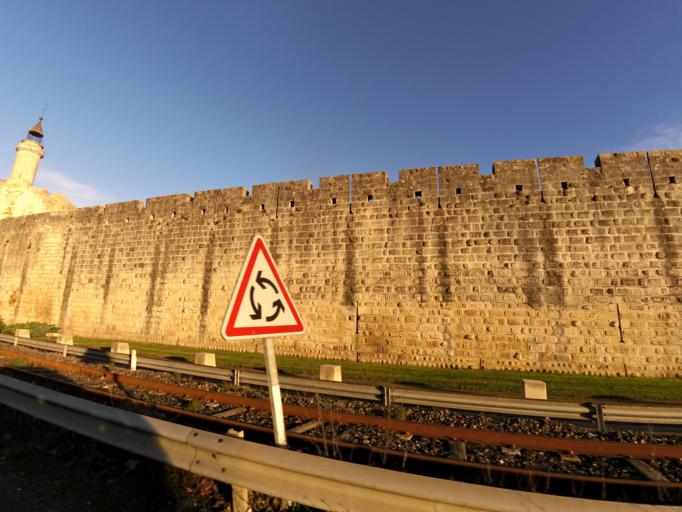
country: FR
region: Languedoc-Roussillon
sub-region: Departement du Gard
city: Aigues-Mortes
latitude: 43.5678
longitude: 4.1887
